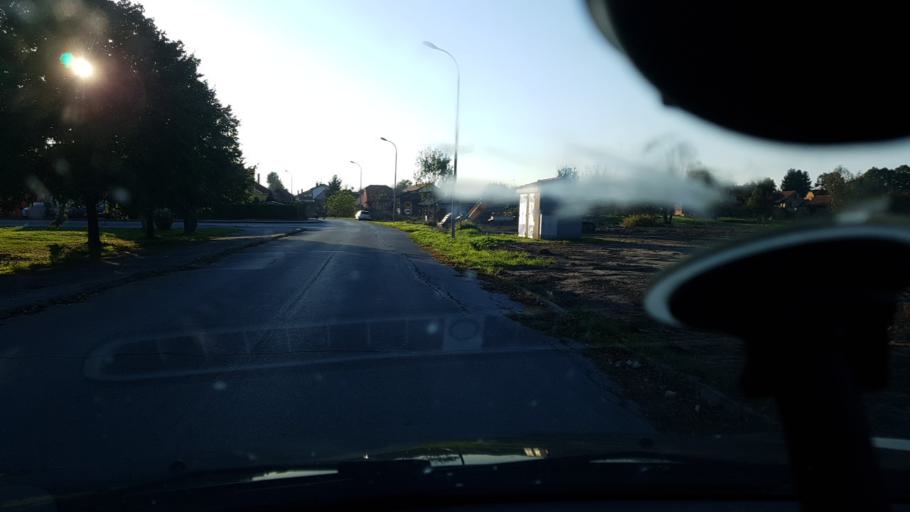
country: HR
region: Koprivnicko-Krizevacka
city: Kalinovac
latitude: 46.0435
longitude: 17.0609
